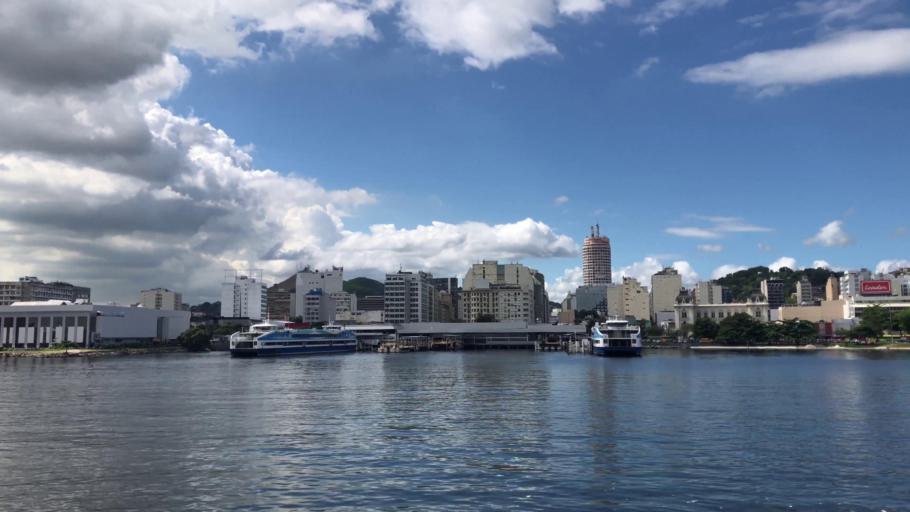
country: BR
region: Rio de Janeiro
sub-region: Niteroi
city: Niteroi
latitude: -22.8921
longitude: -43.1262
